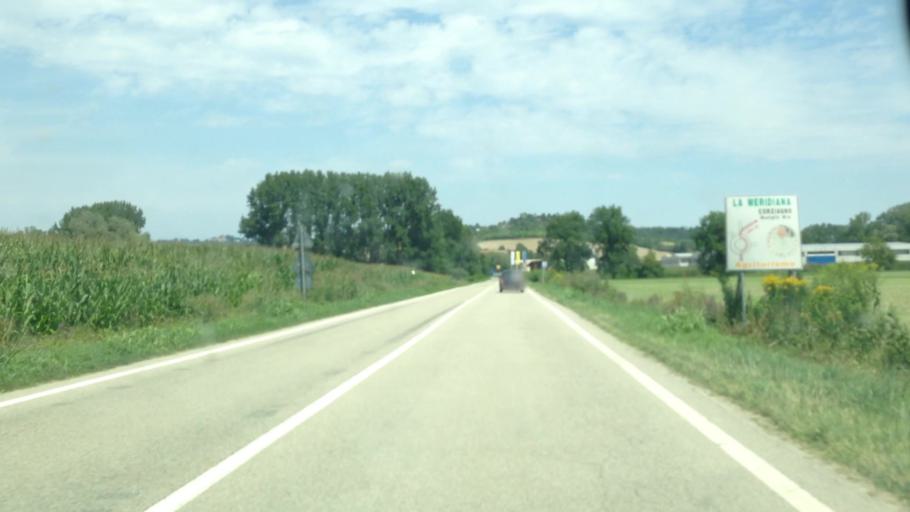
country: IT
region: Piedmont
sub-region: Provincia di Asti
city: Montiglio
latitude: 45.0590
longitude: 8.1128
